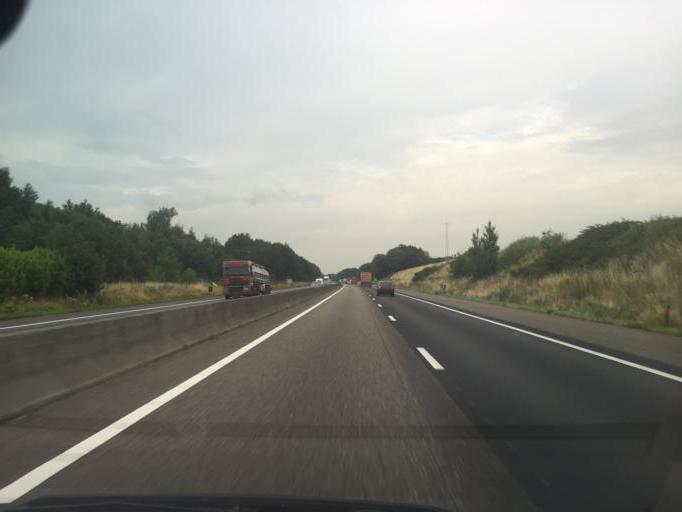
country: NL
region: Limburg
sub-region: Gemeente Peel en Maas
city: Maasbree
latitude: 51.3789
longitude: 6.0066
